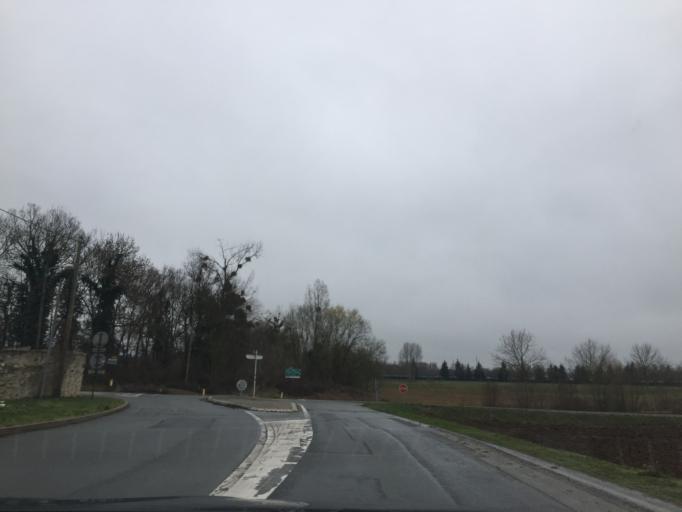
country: FR
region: Ile-de-France
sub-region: Departement de Seine-et-Marne
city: Coupvray
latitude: 48.8833
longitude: 2.7928
